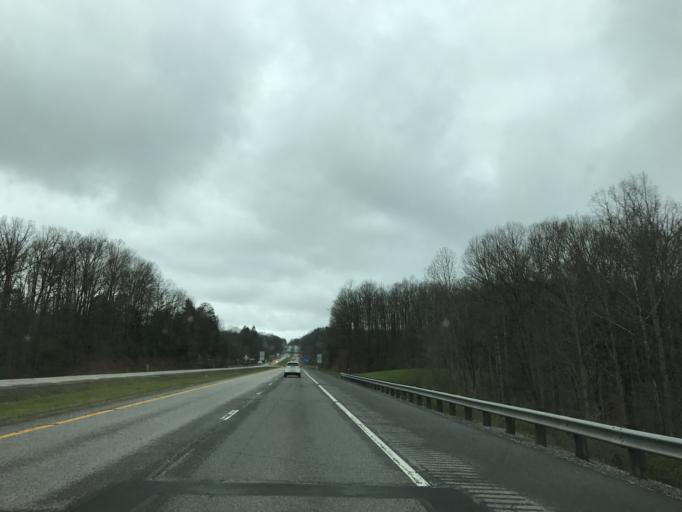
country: US
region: West Virginia
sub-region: Fayette County
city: Fayetteville
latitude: 38.0626
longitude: -81.0953
